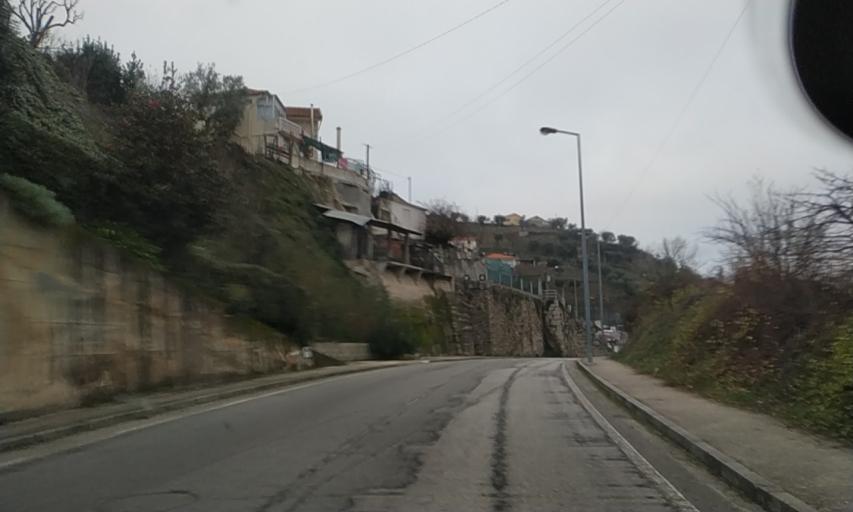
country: PT
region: Viseu
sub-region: Lamego
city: Lamego
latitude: 41.1255
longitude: -7.8043
